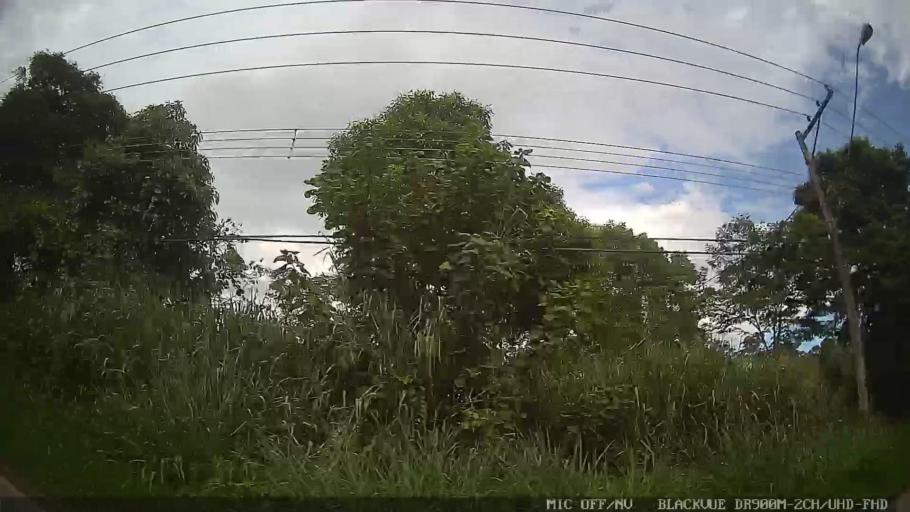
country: BR
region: Sao Paulo
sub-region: Biritiba-Mirim
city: Biritiba Mirim
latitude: -23.5660
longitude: -46.1046
